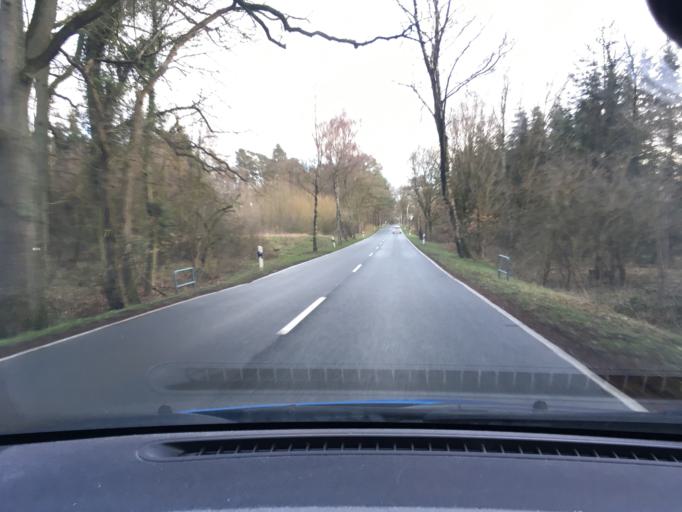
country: DE
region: Lower Saxony
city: Hanstedt
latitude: 53.2255
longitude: 10.0242
